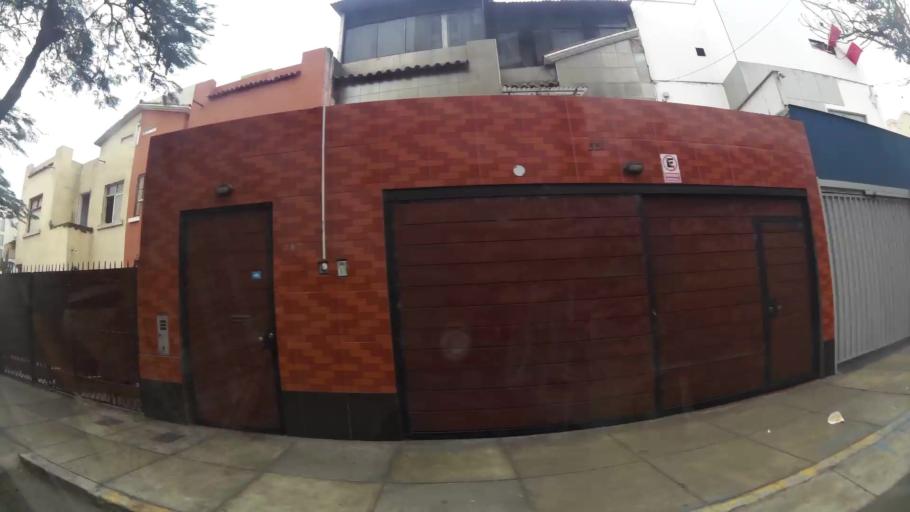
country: PE
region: Lima
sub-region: Lima
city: San Isidro
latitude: -12.1144
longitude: -77.0309
